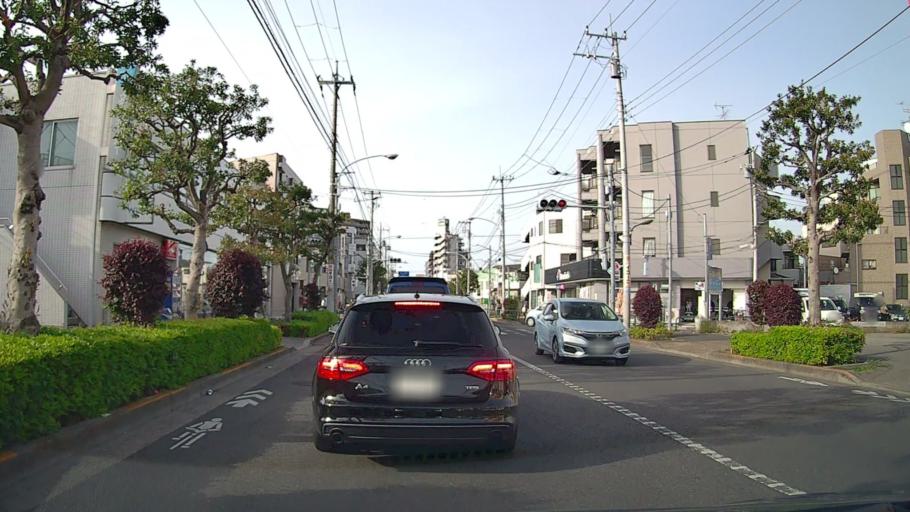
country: JP
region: Saitama
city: Soka
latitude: 35.7936
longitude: 139.7876
